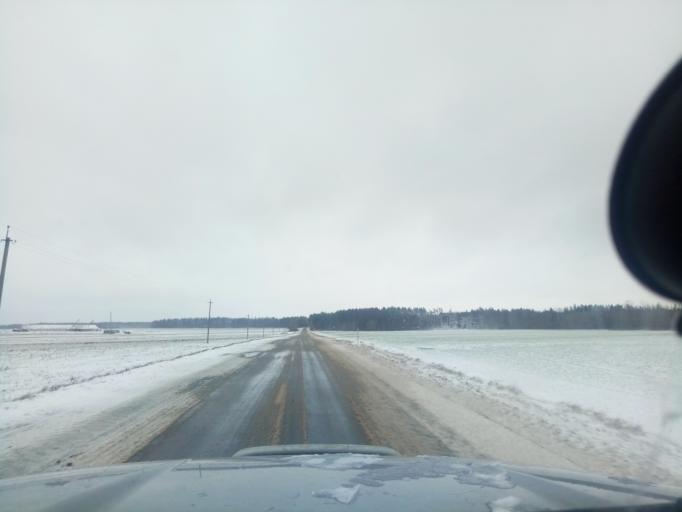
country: BY
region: Minsk
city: Tsimkavichy
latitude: 53.0469
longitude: 26.8614
